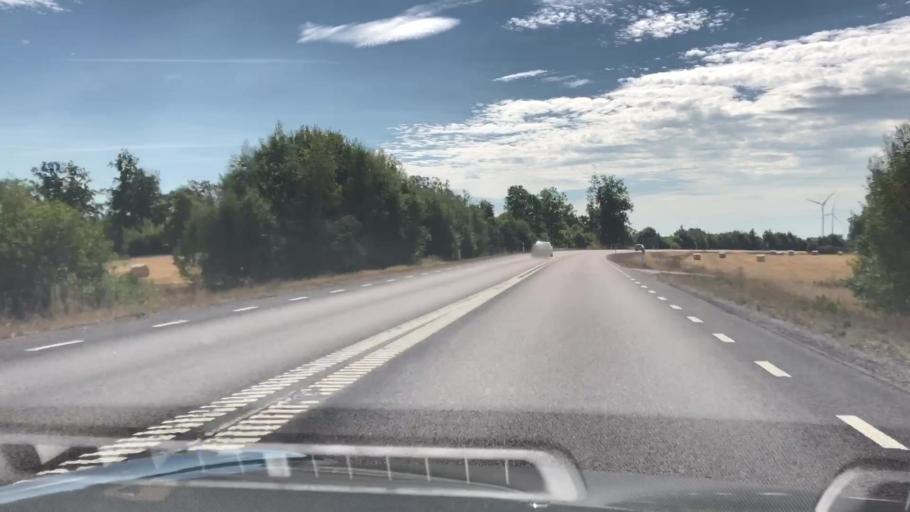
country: SE
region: Kalmar
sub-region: Torsas Kommun
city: Torsas
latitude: 56.4327
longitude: 16.0768
